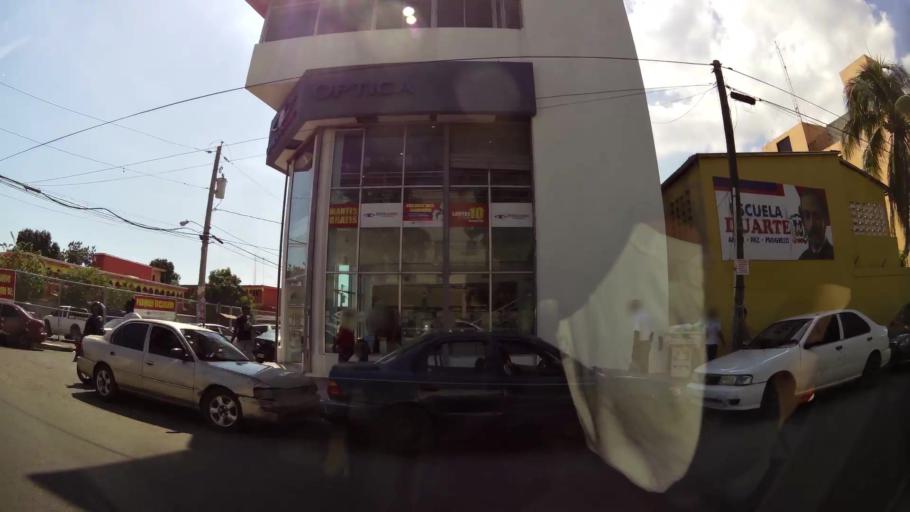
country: DO
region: Nacional
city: Santo Domingo
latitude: 18.4735
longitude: -69.9717
